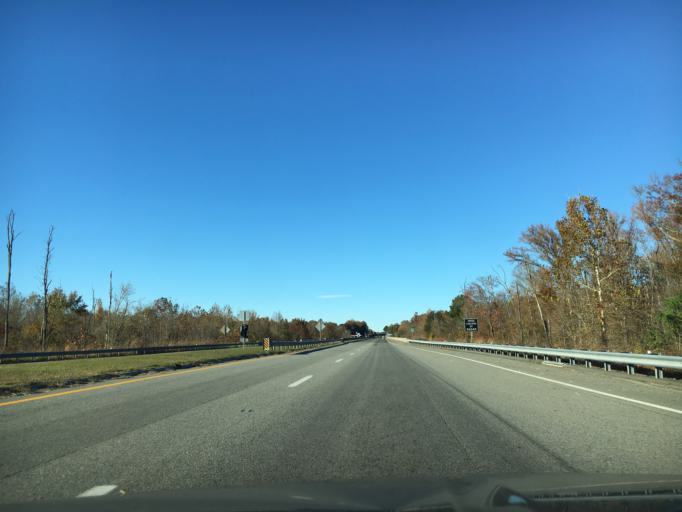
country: US
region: Virginia
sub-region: Halifax County
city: South Boston
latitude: 36.6900
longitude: -78.8871
